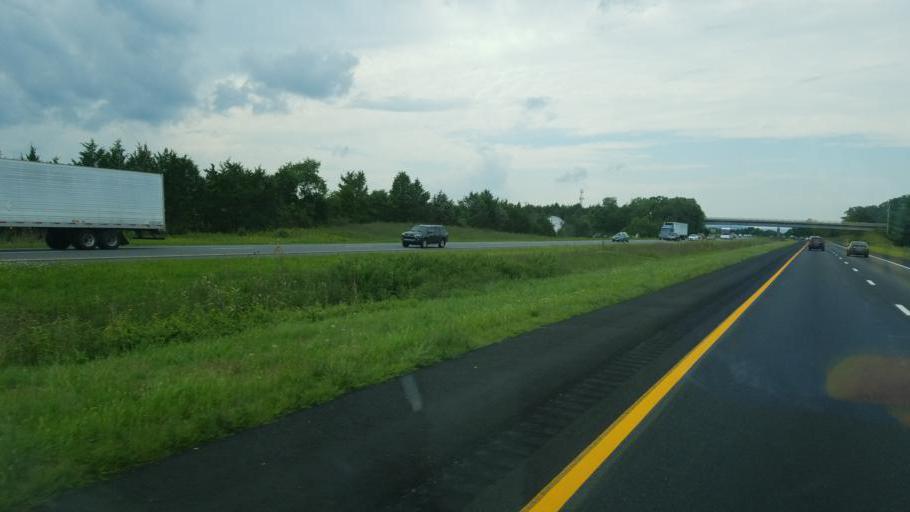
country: US
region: Virginia
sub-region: Frederick County
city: Middletown
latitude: 38.9915
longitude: -78.2470
